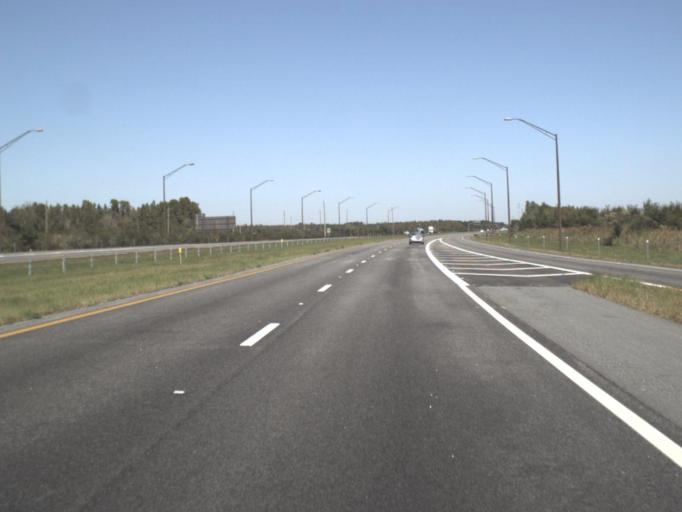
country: US
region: Florida
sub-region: Pasco County
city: Odessa
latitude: 28.1945
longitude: -82.5461
